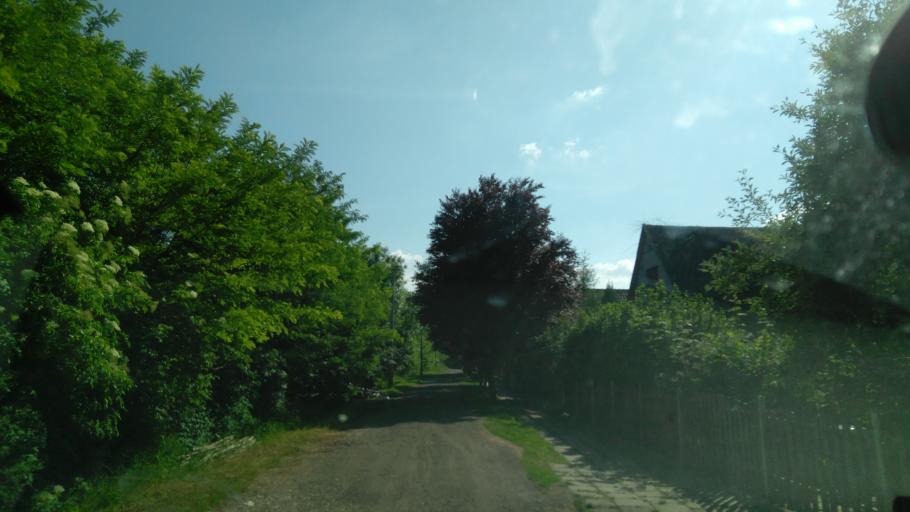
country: HU
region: Bekes
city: Doboz
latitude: 46.6999
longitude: 21.1916
